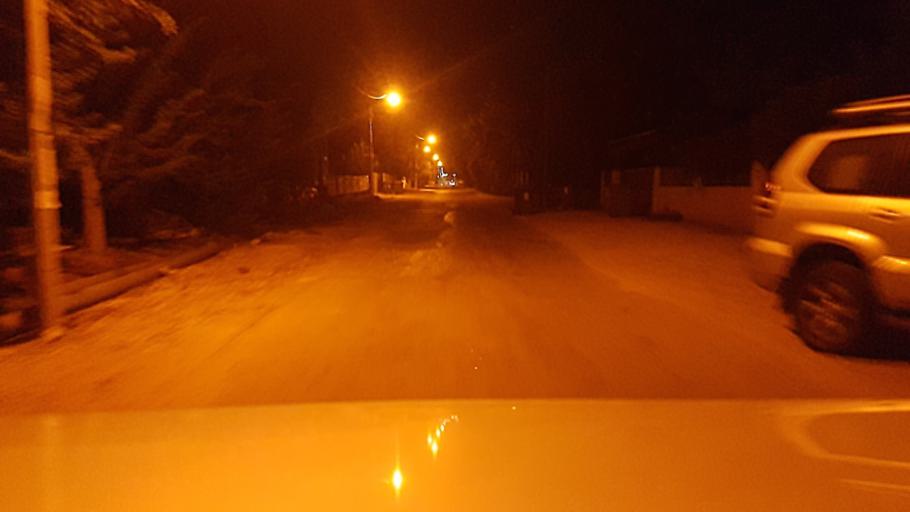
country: IL
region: Central District
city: Nehalim
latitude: 32.0801
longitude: 34.9228
